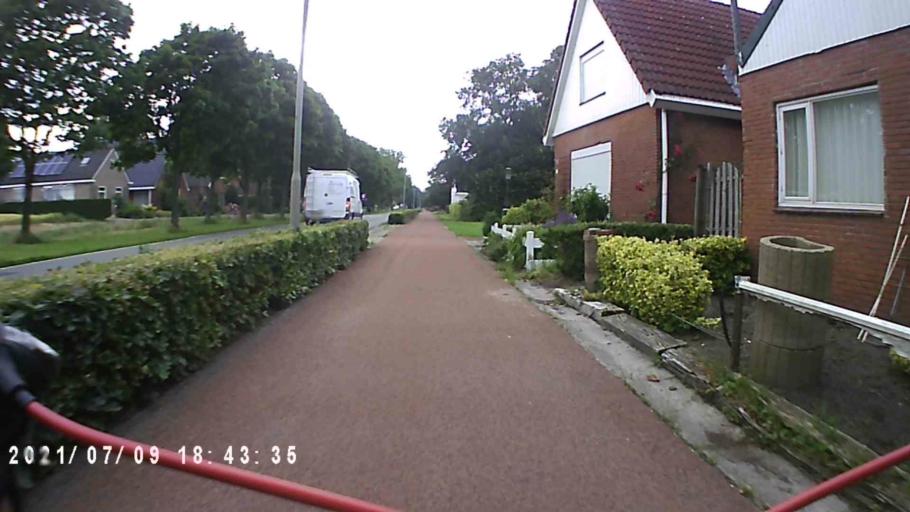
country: NL
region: Groningen
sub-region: Gemeente Veendam
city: Veendam
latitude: 53.0796
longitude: 6.9197
